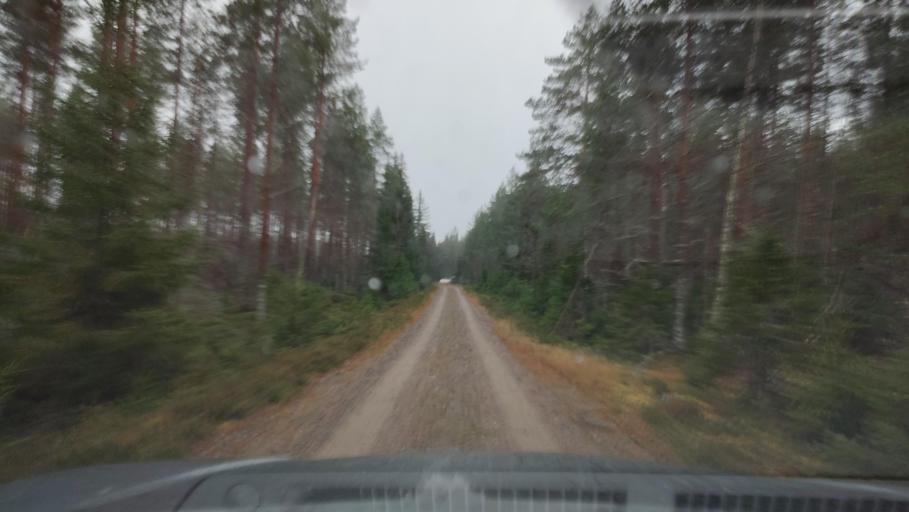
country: FI
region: Southern Ostrobothnia
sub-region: Suupohja
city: Karijoki
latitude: 62.1830
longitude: 21.7331
